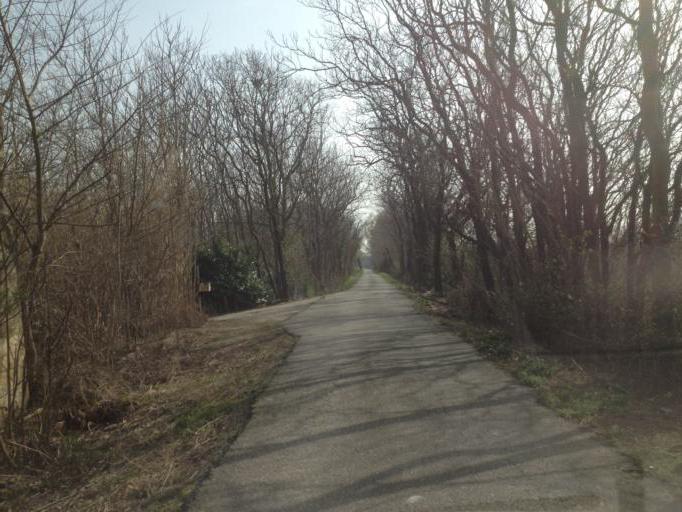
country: FR
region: Provence-Alpes-Cote d'Azur
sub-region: Departement du Vaucluse
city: Bedarrides
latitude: 44.0512
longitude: 4.9282
